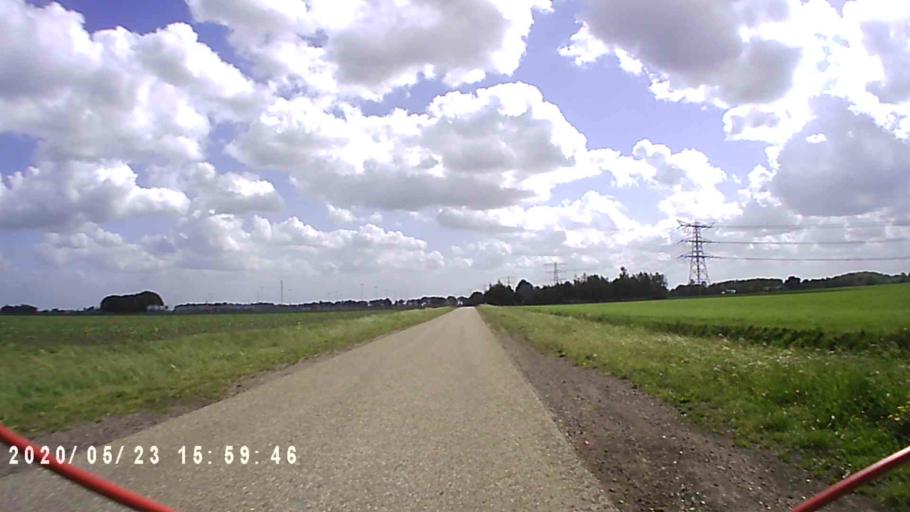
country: NL
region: Groningen
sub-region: Gemeente Delfzijl
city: Delfzijl
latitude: 53.2544
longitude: 6.8998
